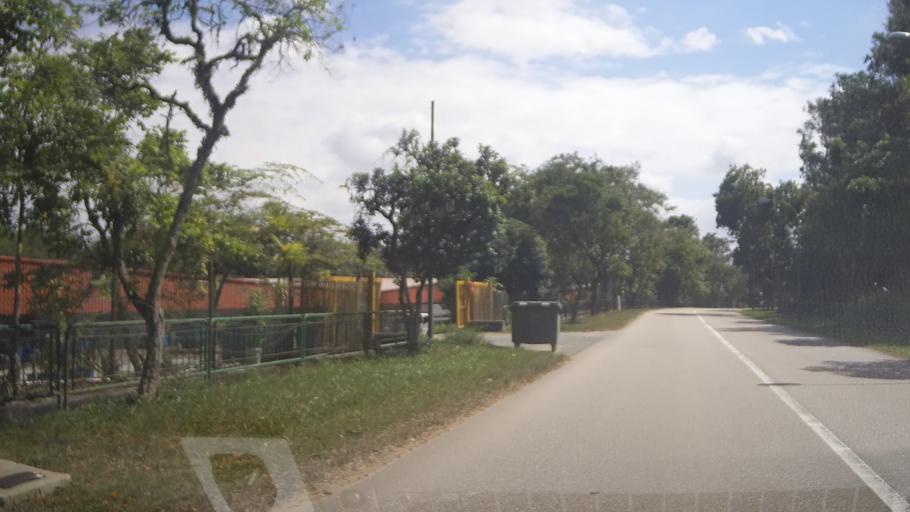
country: MY
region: Johor
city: Johor Bahru
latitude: 1.4310
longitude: 103.7120
